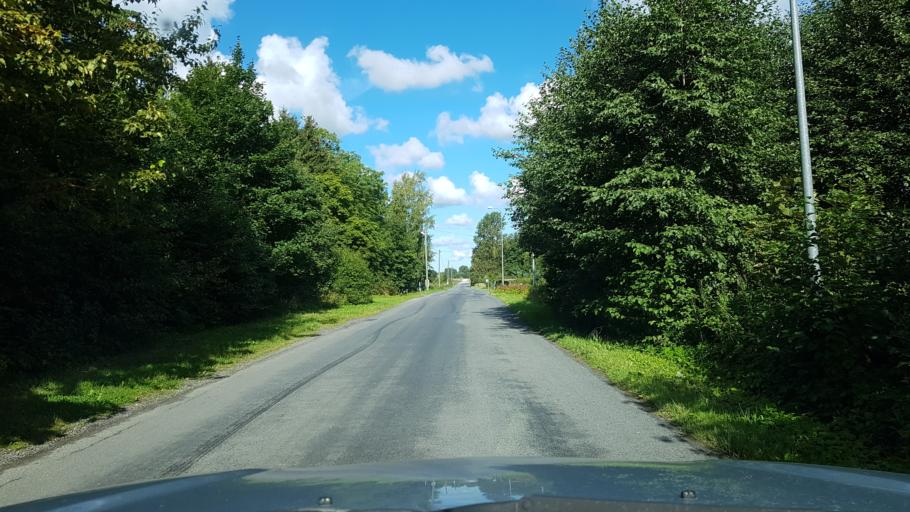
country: EE
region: Harju
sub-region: Kiili vald
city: Kiili
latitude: 59.3716
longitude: 24.8121
